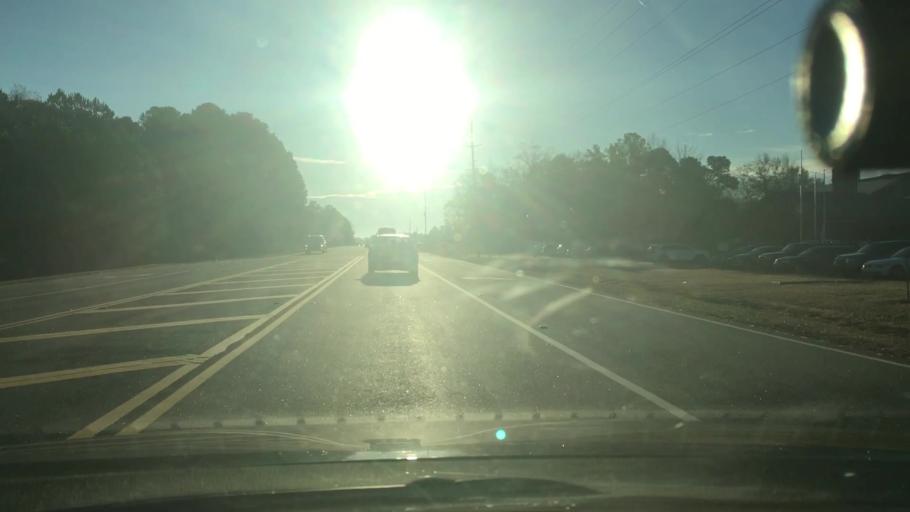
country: US
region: Georgia
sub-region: Coweta County
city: Senoia
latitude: 33.2975
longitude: -84.5887
